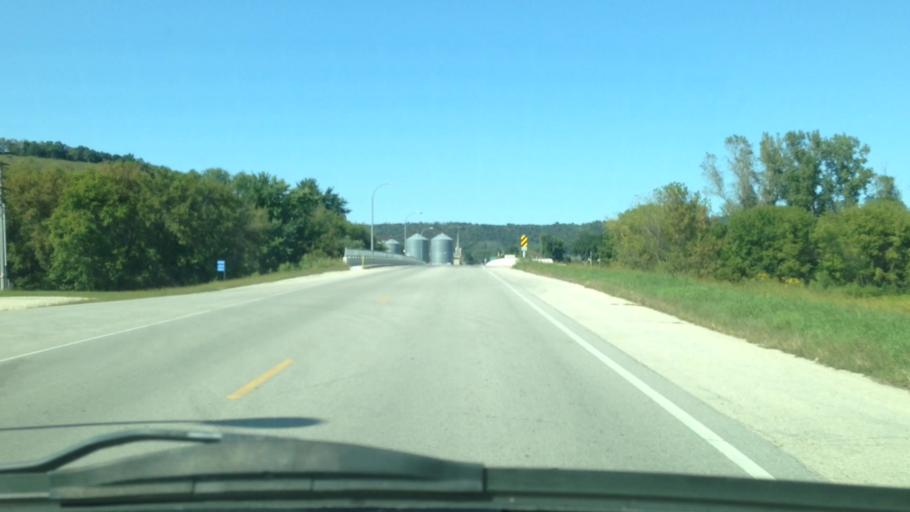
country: US
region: Minnesota
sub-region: Fillmore County
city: Rushford
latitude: 43.8020
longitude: -91.7531
